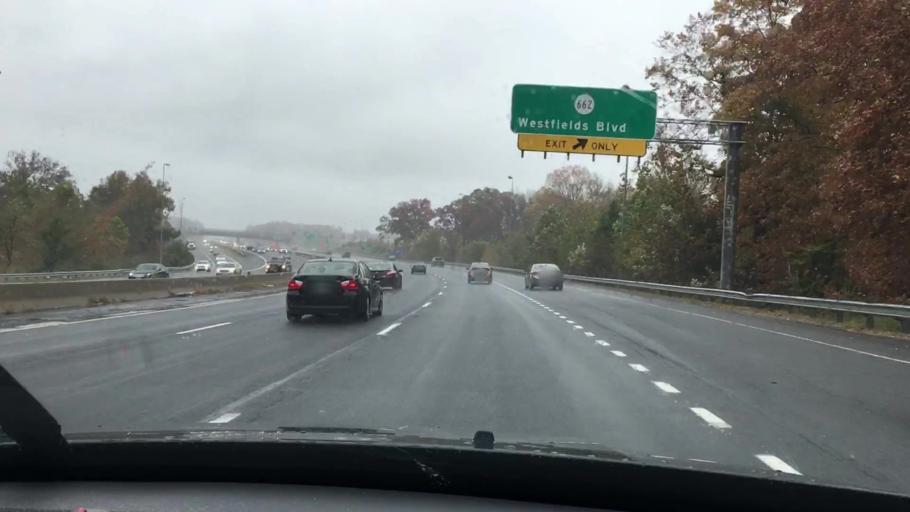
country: US
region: Virginia
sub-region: Fairfax County
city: Chantilly
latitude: 38.8793
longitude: -77.4494
